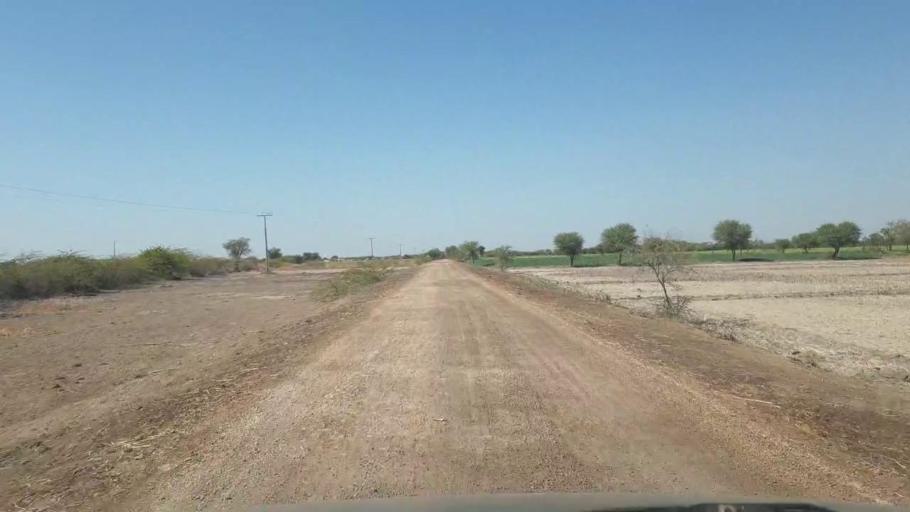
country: PK
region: Sindh
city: Dhoro Naro
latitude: 25.4260
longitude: 69.6186
